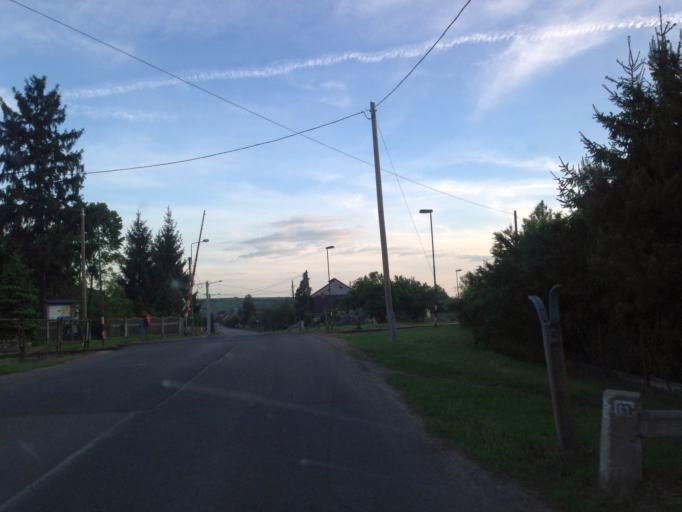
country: HU
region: Nograd
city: Tar
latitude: 47.9566
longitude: 19.7470
